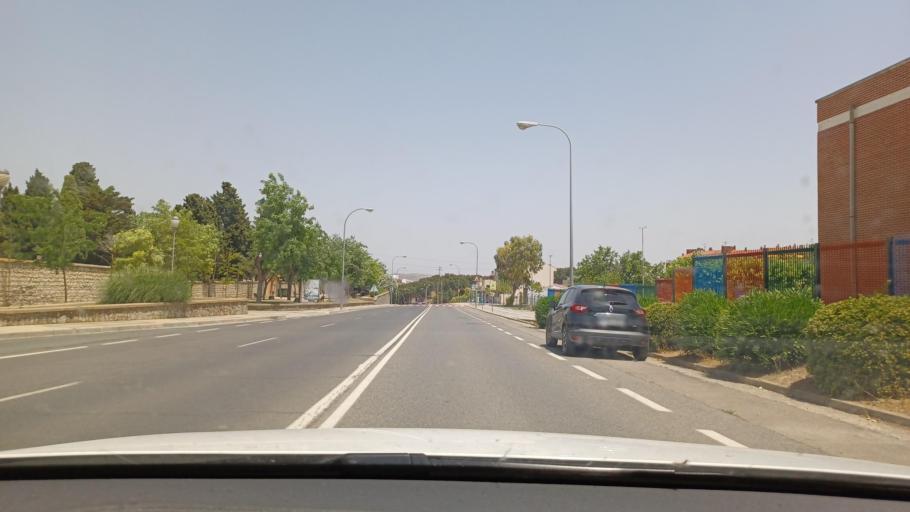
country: ES
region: Navarre
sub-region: Provincia de Navarra
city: Tudela
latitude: 42.0550
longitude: -1.6103
